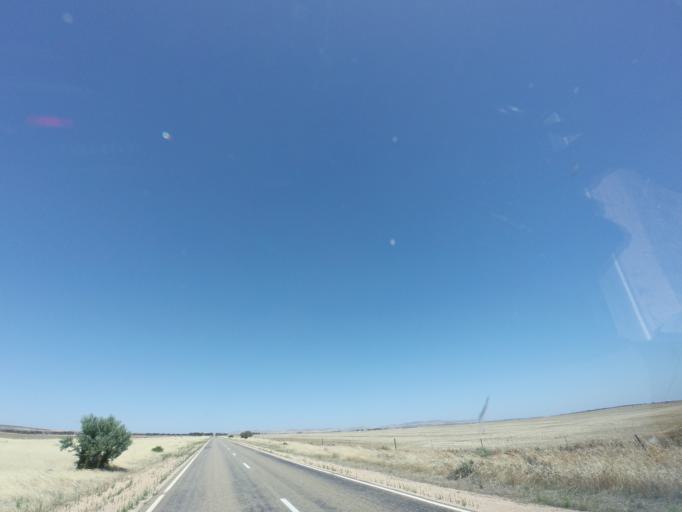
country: AU
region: South Australia
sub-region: Flinders Ranges
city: Quorn
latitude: -32.6930
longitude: 138.3565
